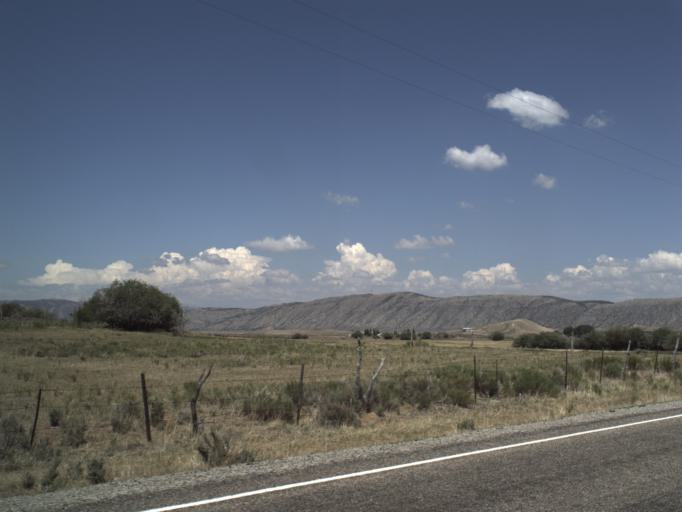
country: US
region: Utah
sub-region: Rich County
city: Randolph
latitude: 41.5228
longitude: -111.1872
